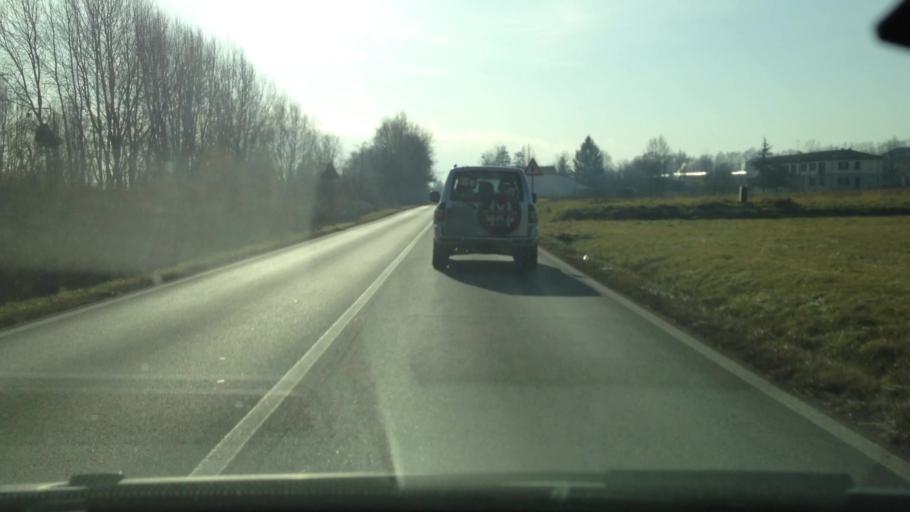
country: IT
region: Piedmont
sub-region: Provincia di Asti
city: Asti
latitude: 44.9343
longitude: 8.2250
